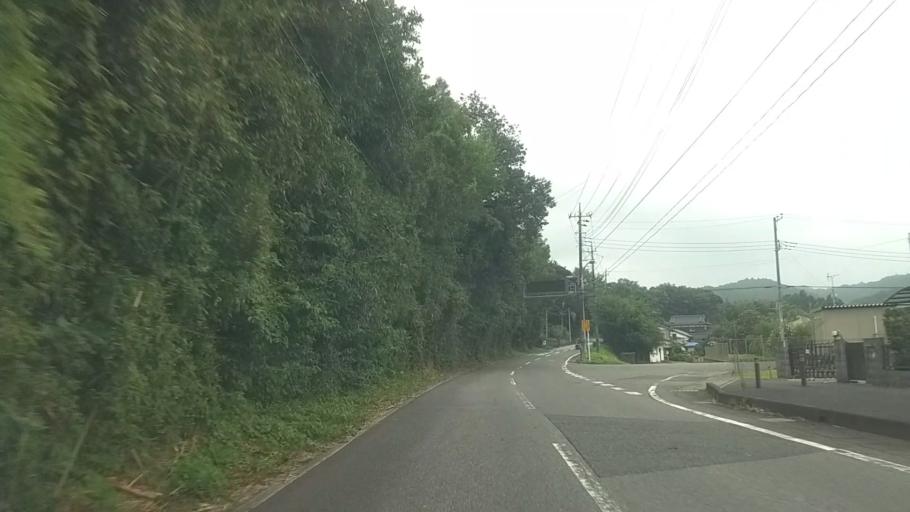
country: JP
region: Chiba
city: Kimitsu
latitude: 35.2332
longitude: 140.0046
